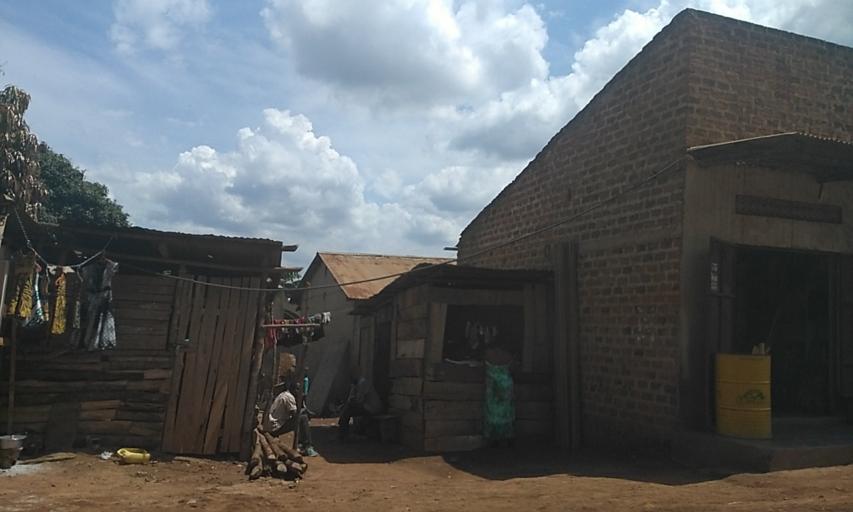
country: UG
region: Central Region
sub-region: Wakiso District
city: Wakiso
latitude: 0.3924
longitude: 32.4643
